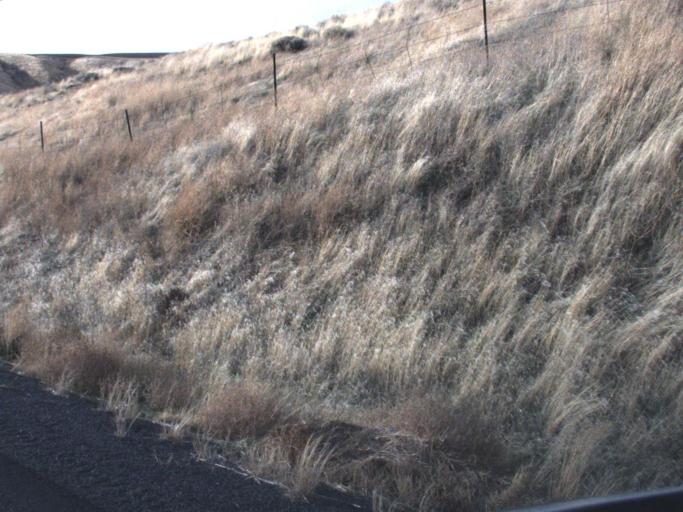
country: US
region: Washington
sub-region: Garfield County
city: Pomeroy
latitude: 46.4750
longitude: -117.6609
